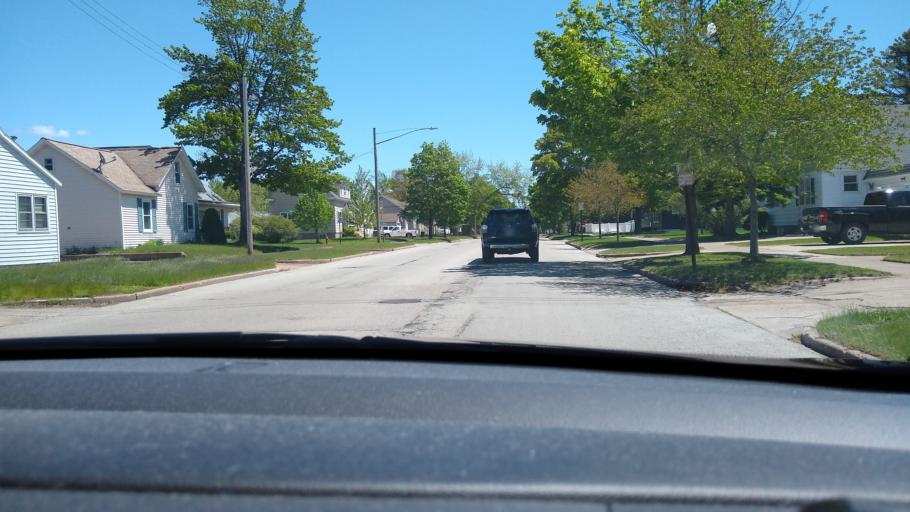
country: US
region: Michigan
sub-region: Delta County
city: Escanaba
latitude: 45.7395
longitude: -87.0734
